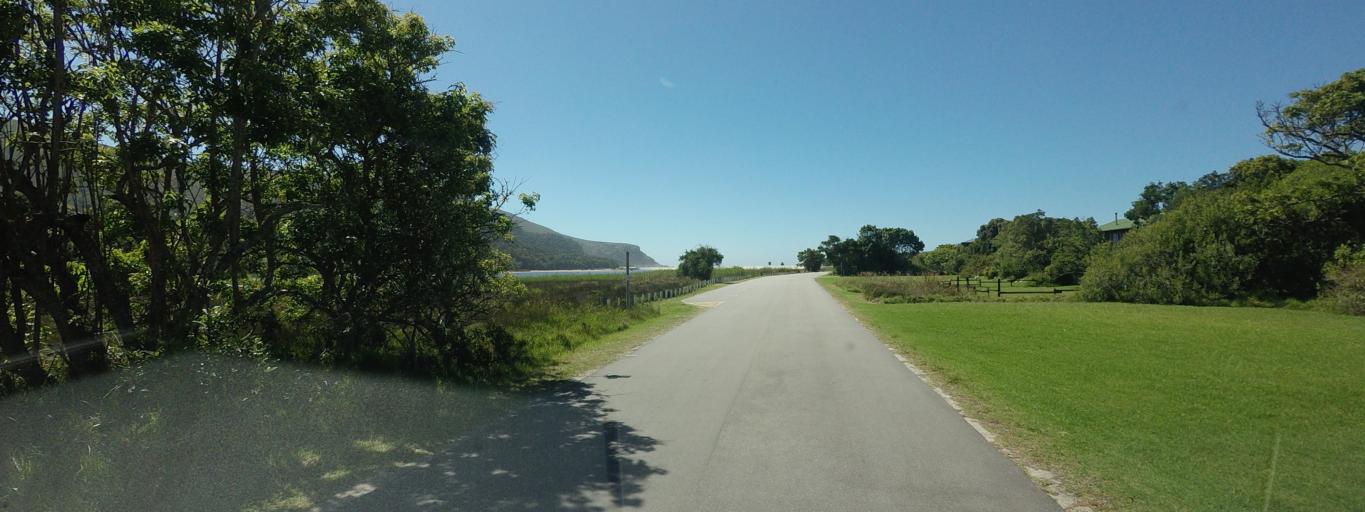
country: ZA
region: Western Cape
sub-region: Eden District Municipality
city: Plettenberg Bay
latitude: -33.9768
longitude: 23.5626
